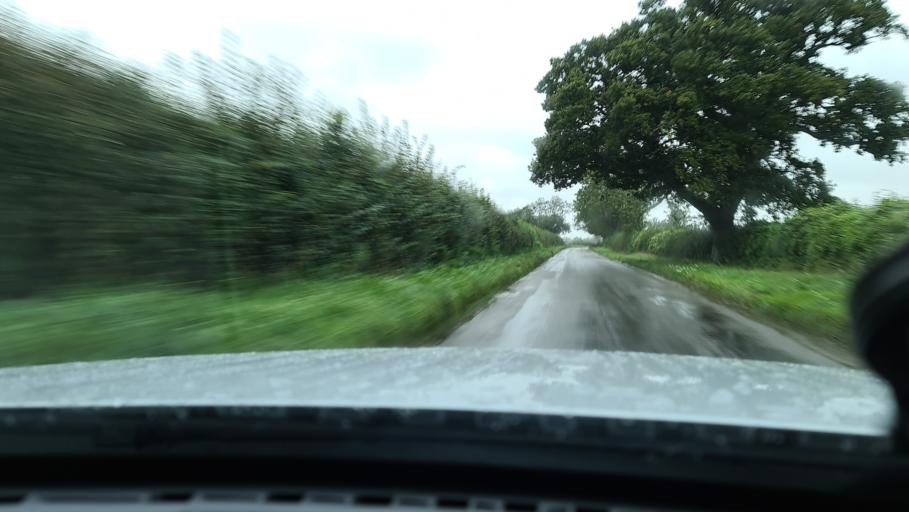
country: GB
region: England
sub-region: Oxfordshire
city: Woodstock
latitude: 51.8991
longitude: -1.3841
